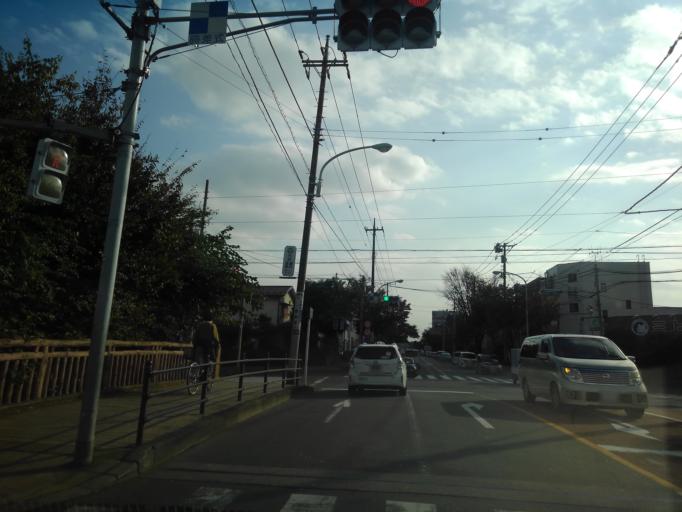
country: JP
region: Tokyo
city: Kokubunji
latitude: 35.7135
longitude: 139.4967
